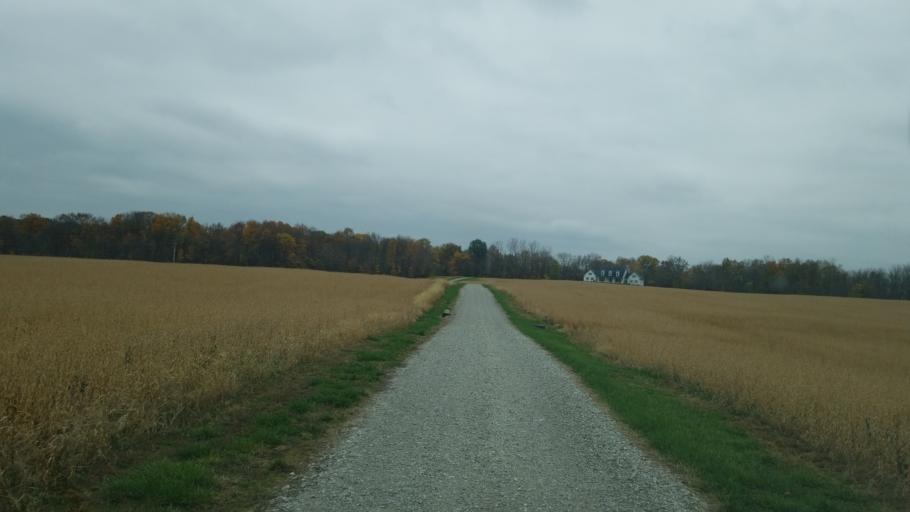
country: US
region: Ohio
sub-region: Knox County
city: Centerburg
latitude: 40.4328
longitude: -82.6868
